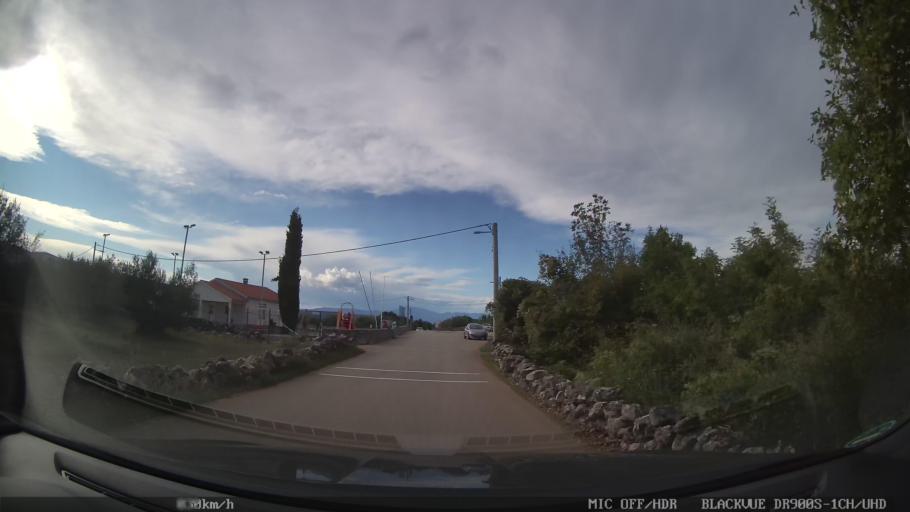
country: HR
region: Primorsko-Goranska
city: Njivice
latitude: 45.0810
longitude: 14.4455
